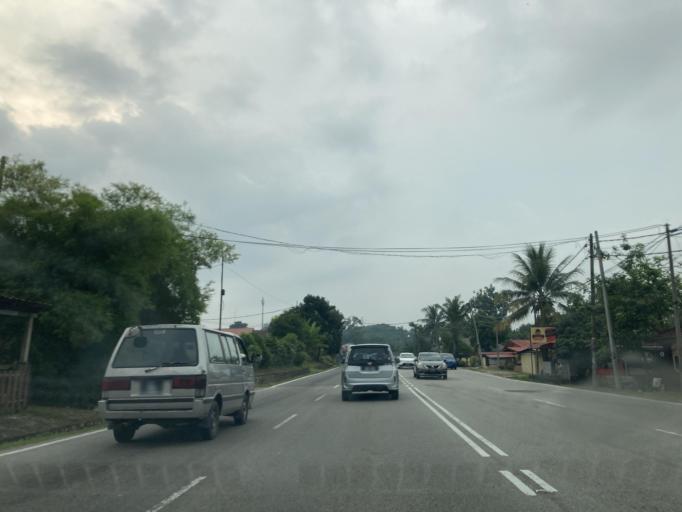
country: MY
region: Selangor
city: Kuang
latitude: 3.2146
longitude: 101.5334
